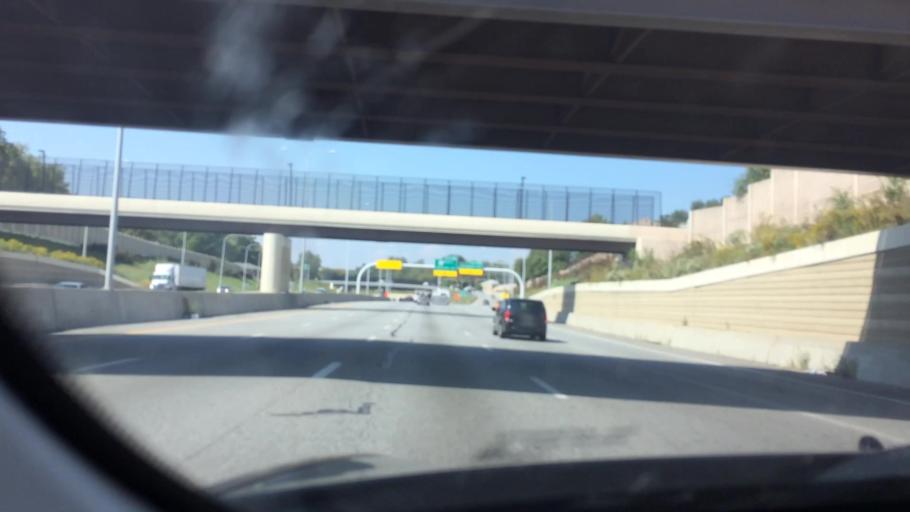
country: US
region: Ohio
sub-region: Lucas County
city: Toledo
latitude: 41.6834
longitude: -83.5992
